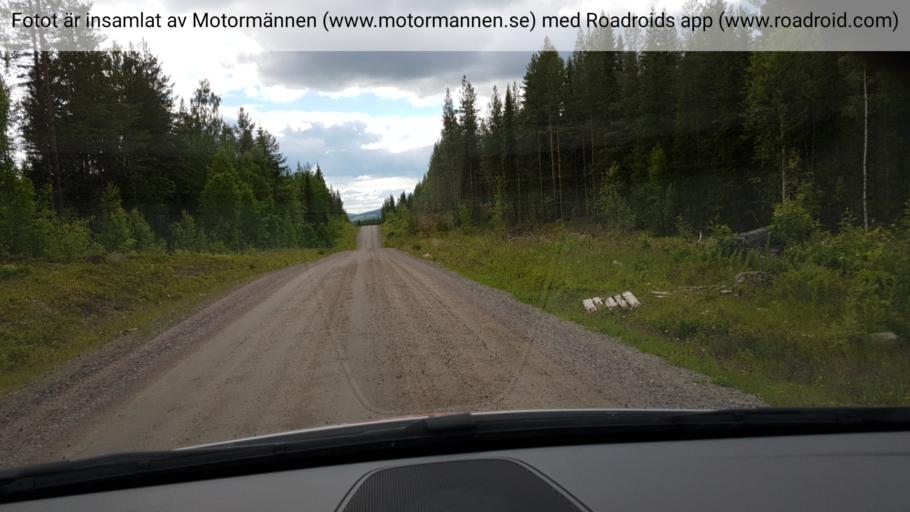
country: SE
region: Vaesterbotten
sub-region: Dorotea Kommun
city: Dorotea
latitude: 63.9322
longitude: 16.1552
